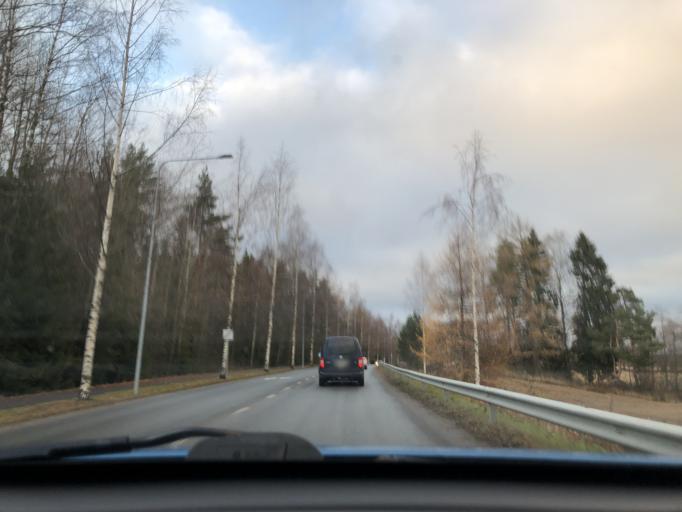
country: FI
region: Pirkanmaa
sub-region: Tampere
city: Kangasala
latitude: 61.4680
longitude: 24.0627
